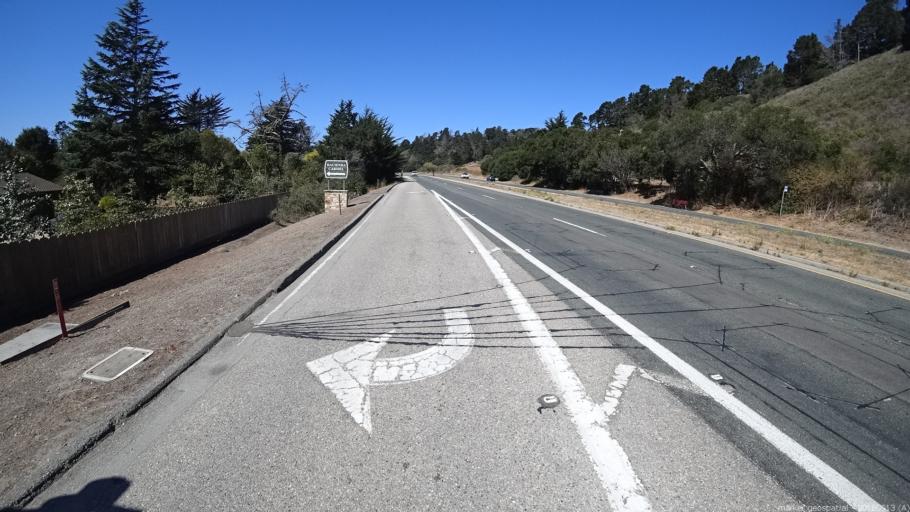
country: US
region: California
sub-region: Monterey County
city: Carmel-by-the-Sea
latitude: 36.5417
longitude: -121.8804
